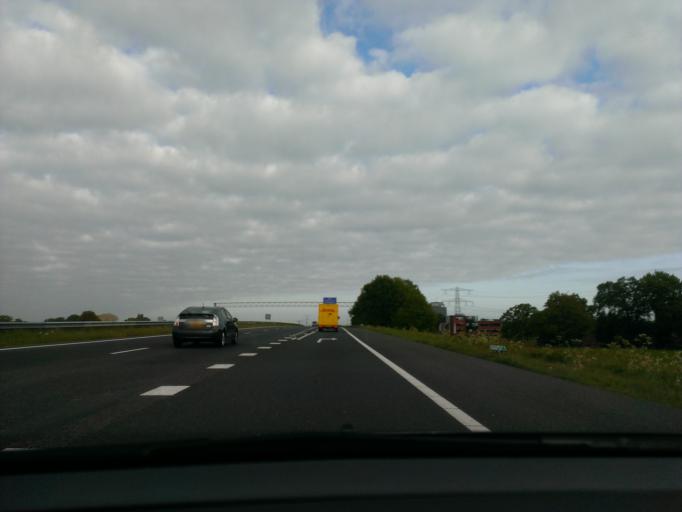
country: NL
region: Overijssel
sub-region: Gemeente Almelo
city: Almelo
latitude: 52.3219
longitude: 6.6568
